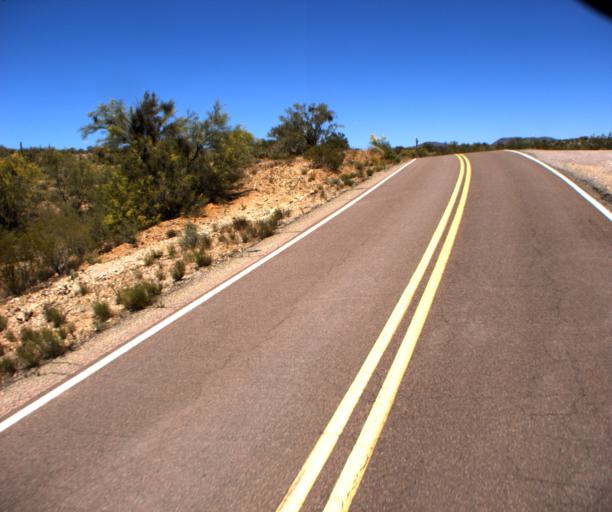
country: US
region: Arizona
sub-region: Yavapai County
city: Bagdad
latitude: 34.4494
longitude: -113.2421
